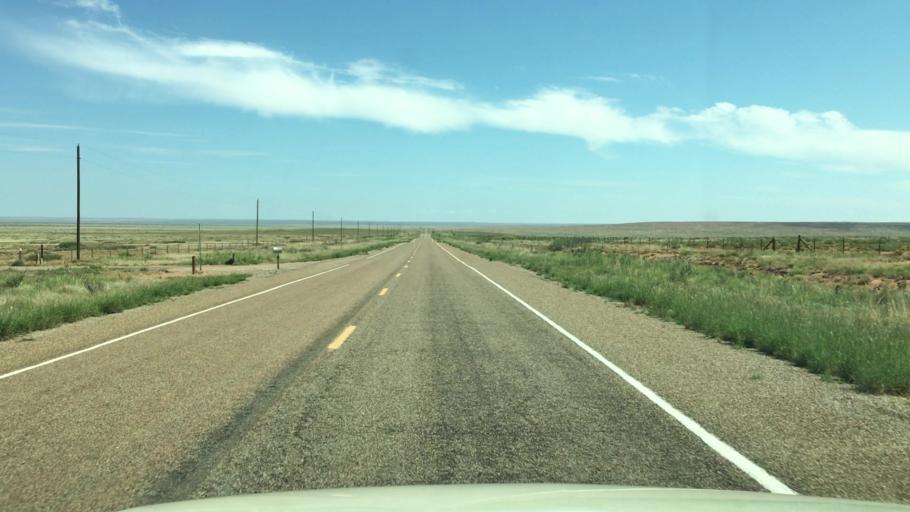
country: US
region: New Mexico
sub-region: De Baca County
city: Fort Sumner
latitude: 33.9912
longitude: -104.5702
